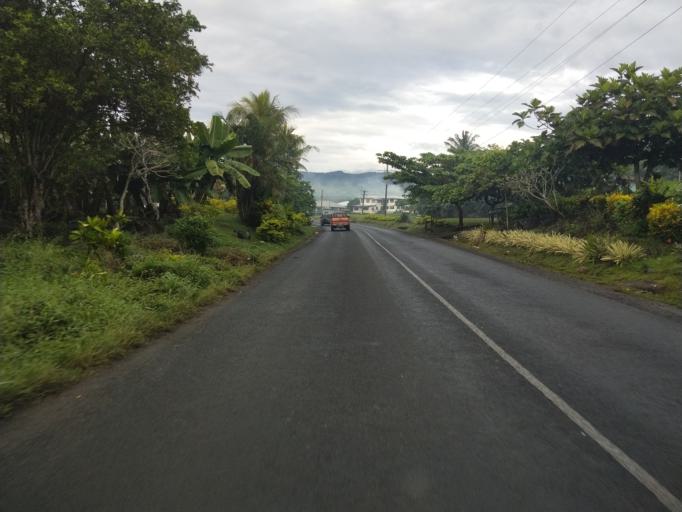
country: WS
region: Tuamasaga
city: Vaiusu
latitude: -13.8134
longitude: -171.8094
